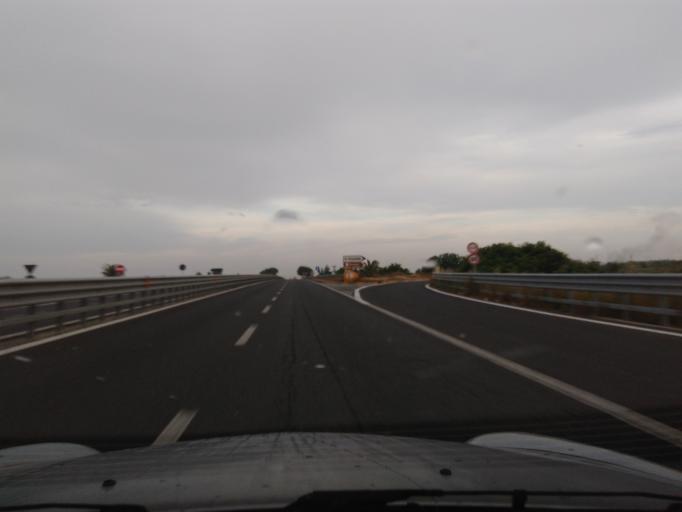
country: IT
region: Apulia
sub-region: Provincia di Bari
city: Giovinazzo
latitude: 41.1816
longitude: 16.6443
